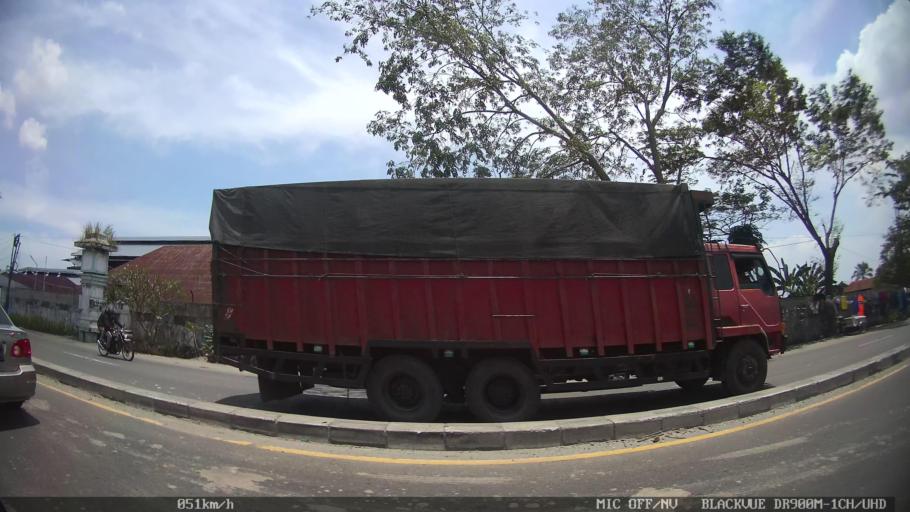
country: ID
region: North Sumatra
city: Binjai
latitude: 3.6029
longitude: 98.5378
